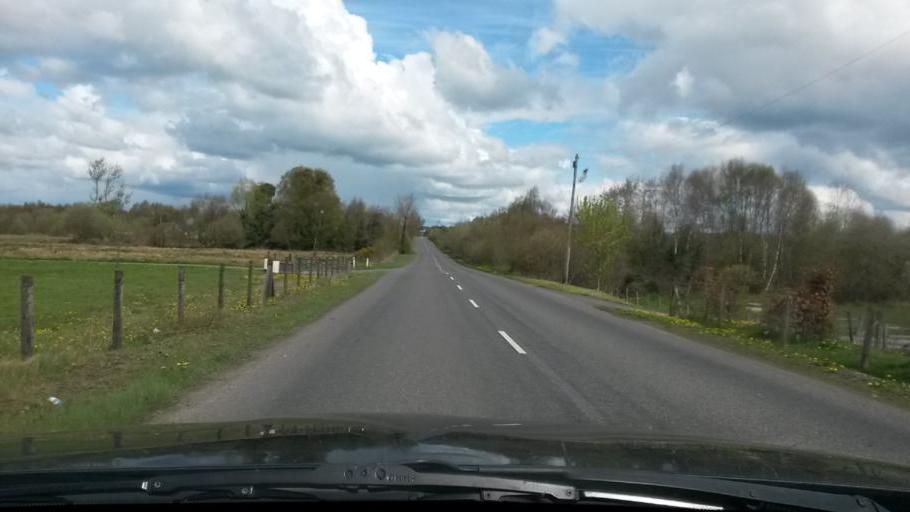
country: GB
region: Northern Ireland
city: Lisnaskea
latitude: 54.2232
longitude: -7.4610
